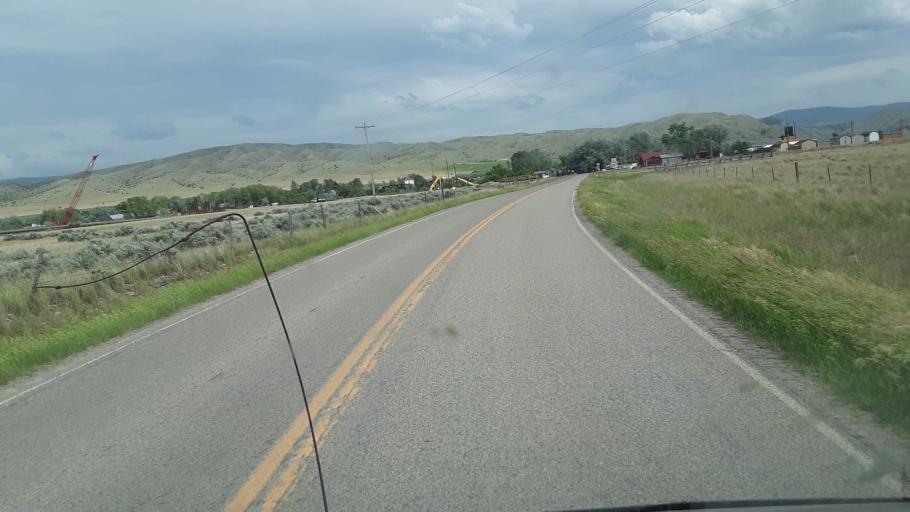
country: US
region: Montana
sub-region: Broadwater County
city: Townsend
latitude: 46.1734
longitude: -111.4506
